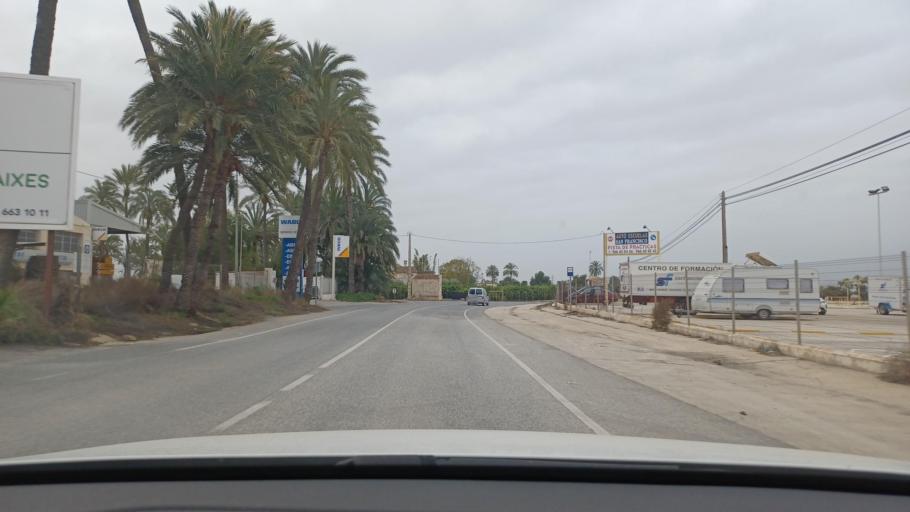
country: ES
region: Valencia
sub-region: Provincia de Alicante
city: Elche
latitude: 38.2396
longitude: -0.7110
